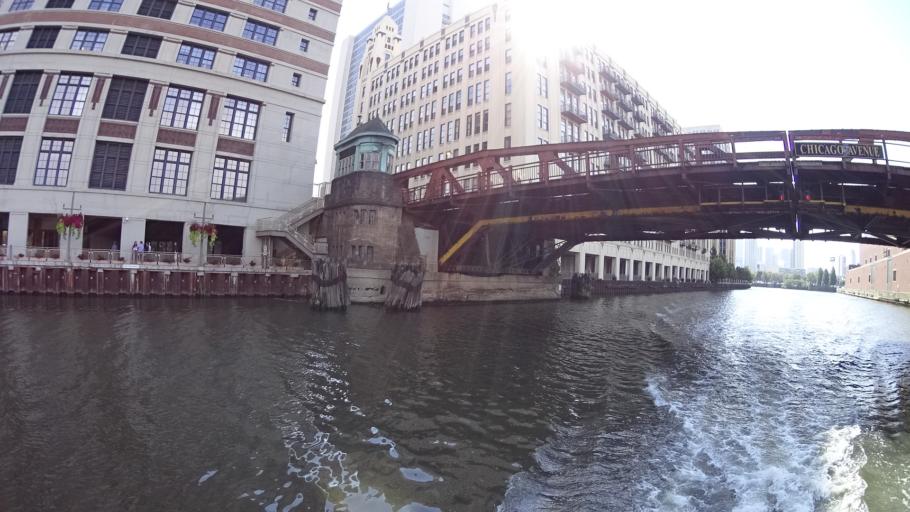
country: US
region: Illinois
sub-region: Cook County
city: Chicago
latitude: 41.8969
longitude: -87.6439
